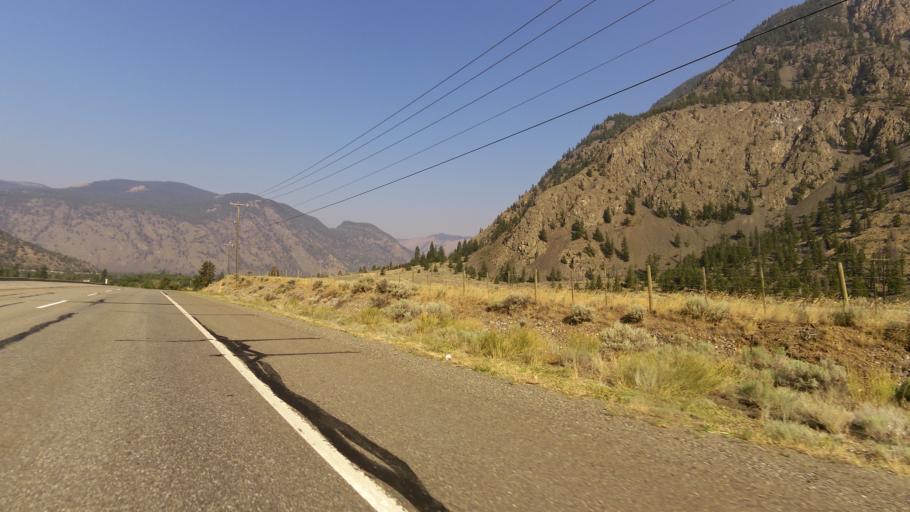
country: CA
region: British Columbia
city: Oliver
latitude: 49.2204
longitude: -119.9460
